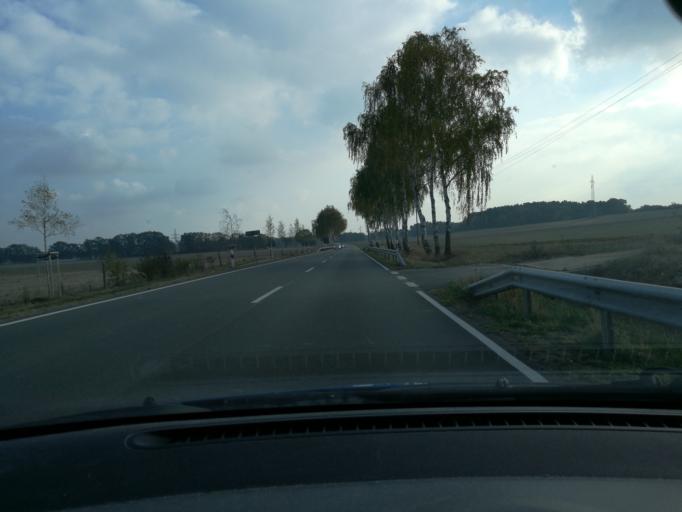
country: DE
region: Lower Saxony
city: Dannenberg
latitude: 53.0983
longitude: 11.0603
